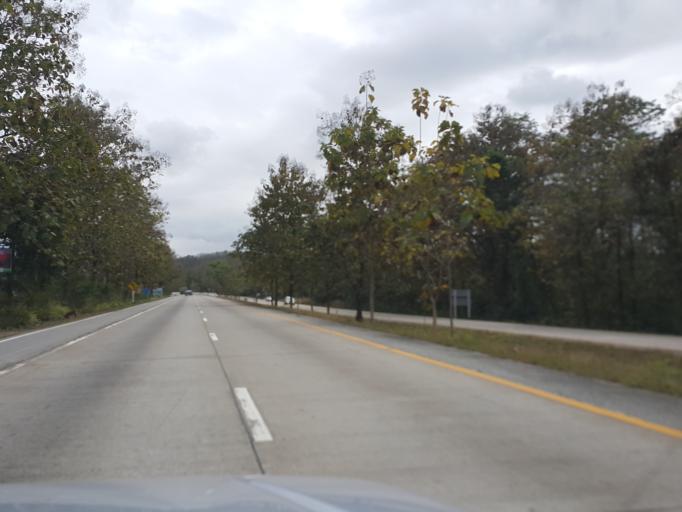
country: TH
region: Lamphun
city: Mae Tha
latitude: 18.5123
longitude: 99.0957
